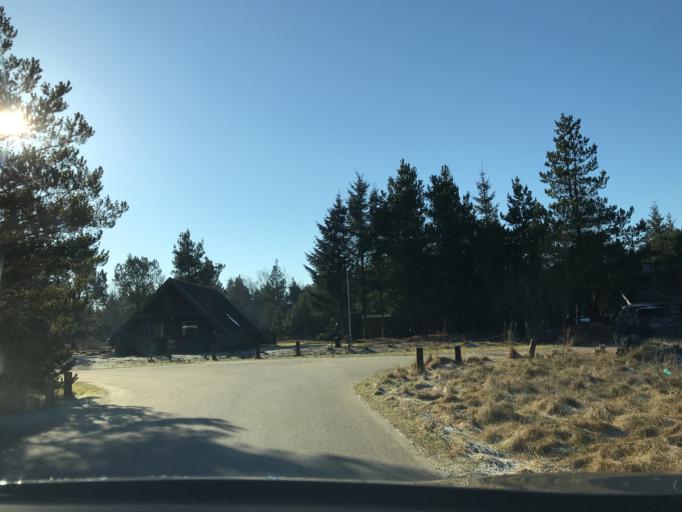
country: DK
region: South Denmark
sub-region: Varde Kommune
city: Oksbol
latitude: 55.7762
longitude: 8.2422
